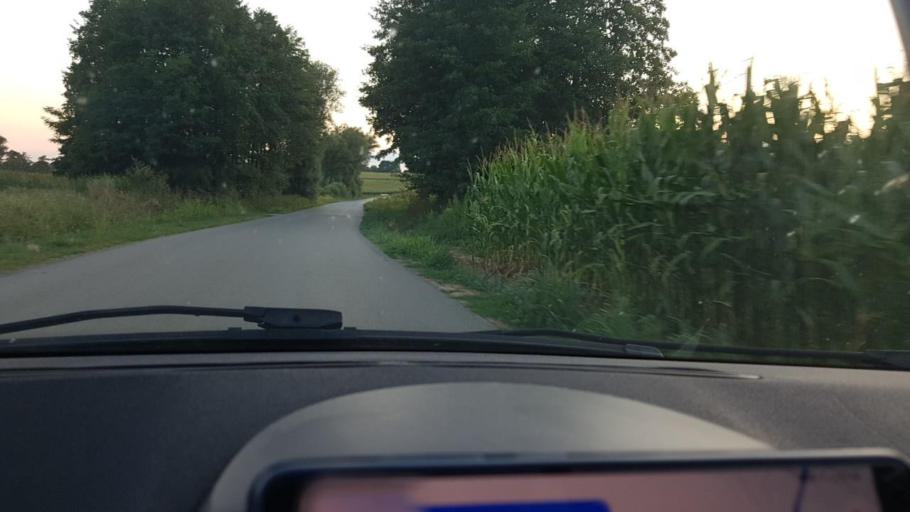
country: HR
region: Bjelovarsko-Bilogorska
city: Zdralovi
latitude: 45.8605
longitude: 16.9897
